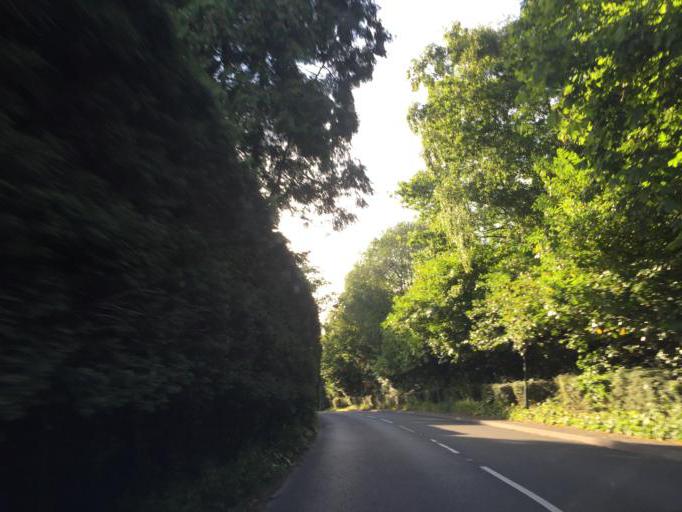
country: GB
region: England
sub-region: East Sussex
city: Wadhurst
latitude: 51.0688
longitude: 0.3243
